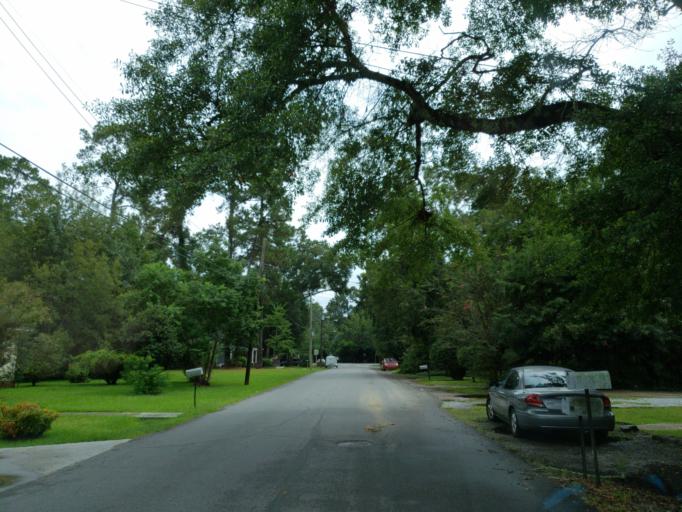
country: US
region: Mississippi
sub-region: Forrest County
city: Hattiesburg
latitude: 31.3186
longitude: -89.3131
